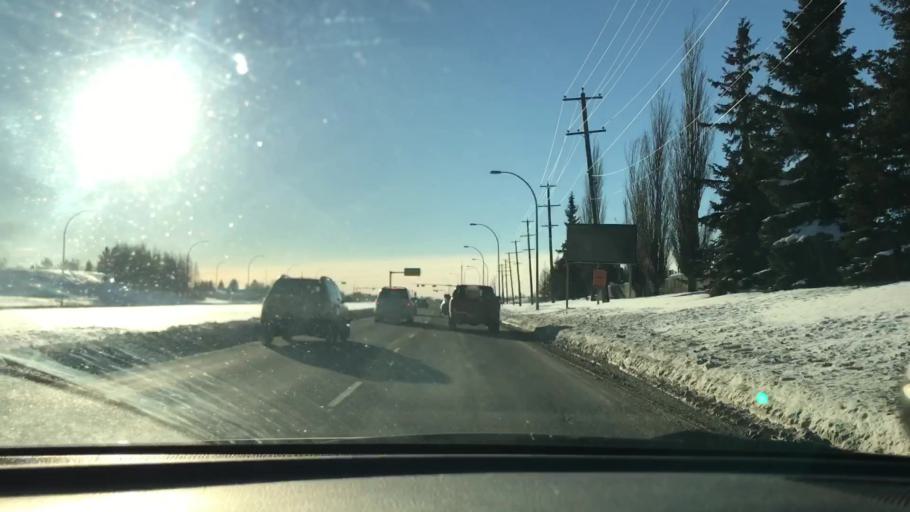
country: CA
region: Alberta
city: Edmonton
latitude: 53.4859
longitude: -113.4674
